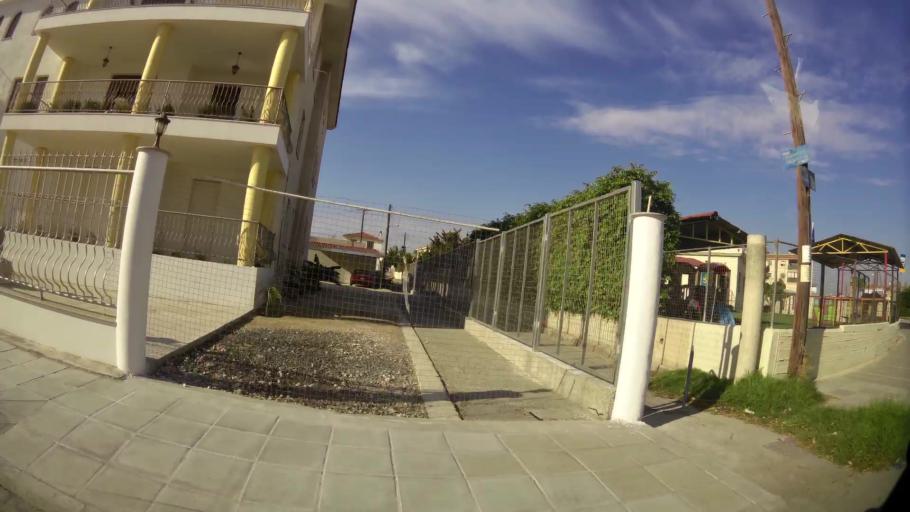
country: CY
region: Larnaka
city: Aradippou
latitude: 34.9510
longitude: 33.5990
